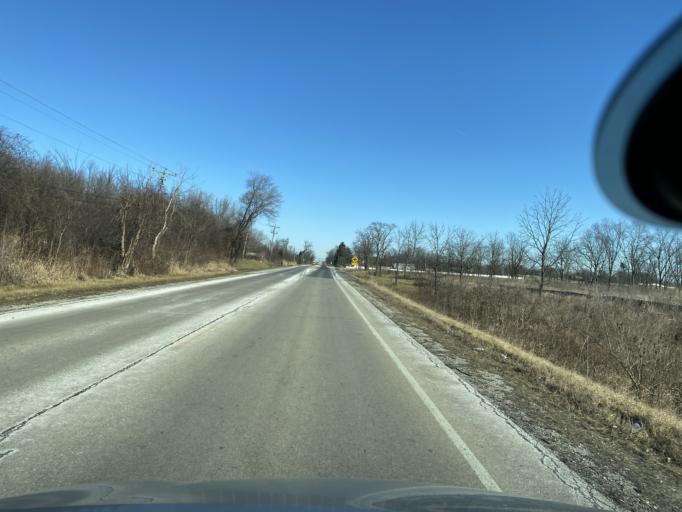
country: US
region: Illinois
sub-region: Will County
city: Lockport
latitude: 41.6174
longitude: -88.0340
